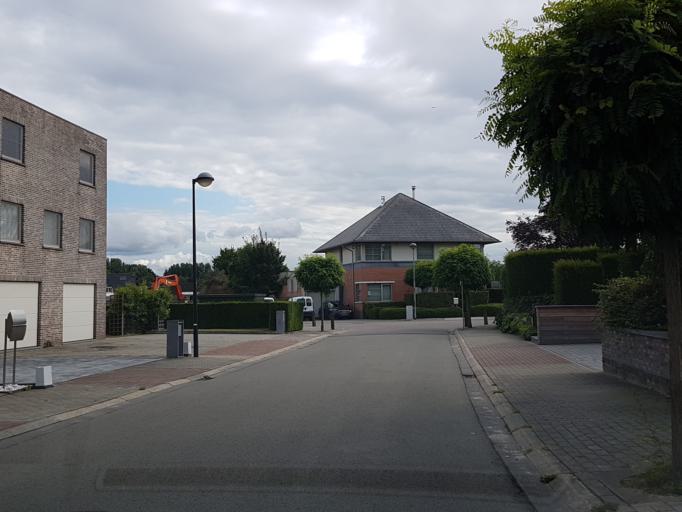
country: BE
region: Flanders
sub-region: Provincie Vlaams-Brabant
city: Kortenberg
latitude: 50.8830
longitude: 4.5109
